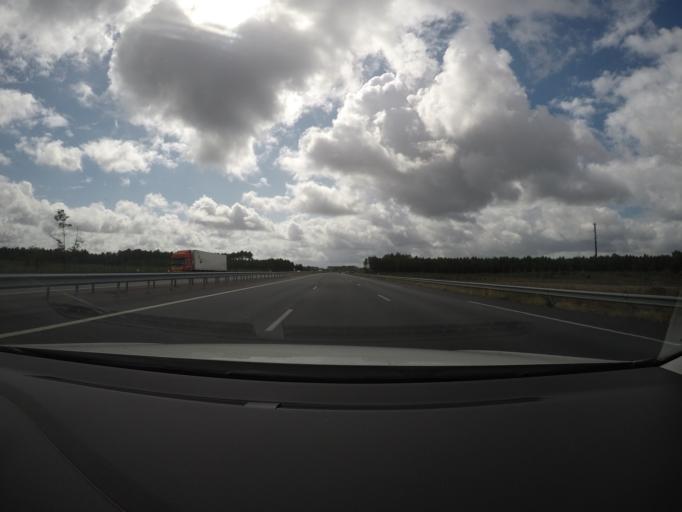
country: FR
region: Aquitaine
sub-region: Departement de la Gironde
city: Belin-Beliet
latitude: 44.4092
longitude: -0.8189
